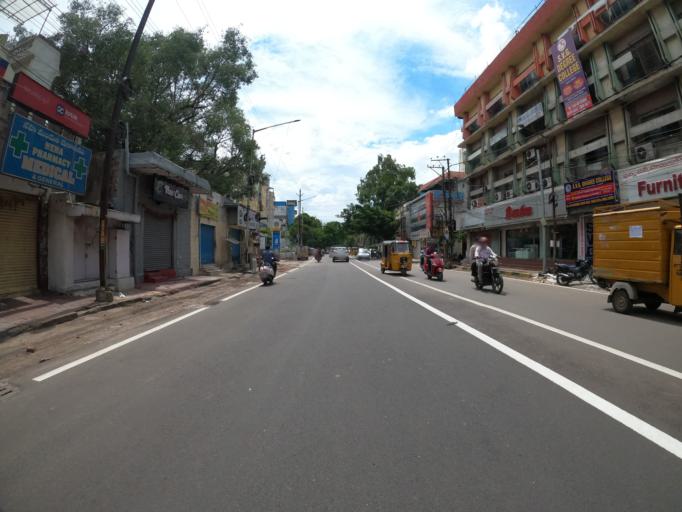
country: IN
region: Telangana
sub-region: Hyderabad
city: Hyderabad
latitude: 17.3992
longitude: 78.4803
